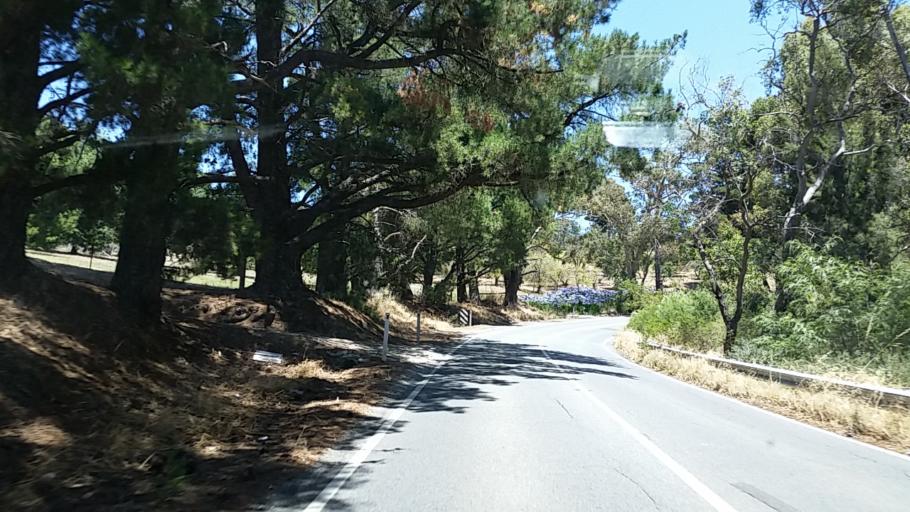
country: AU
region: South Australia
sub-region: Tea Tree Gully
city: Golden Grove
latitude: -34.8235
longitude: 138.7712
